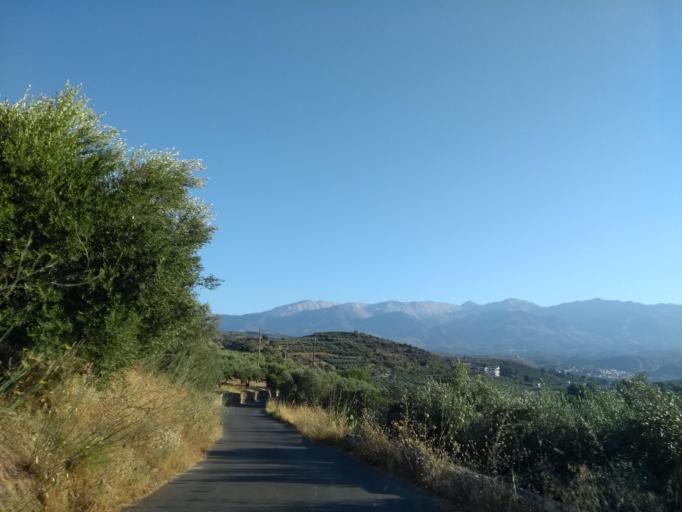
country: GR
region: Crete
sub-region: Nomos Chanias
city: Kalivai
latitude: 35.4449
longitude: 24.1723
